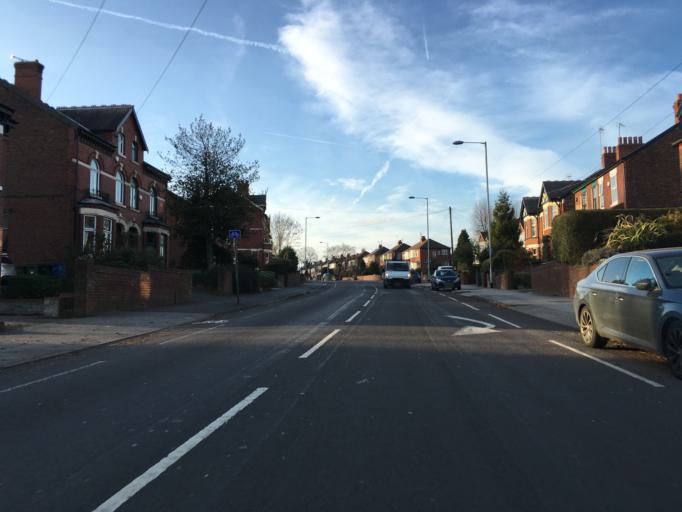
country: GB
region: England
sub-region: Borough of Stockport
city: Cheadle Heath
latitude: 53.4123
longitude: -2.1855
